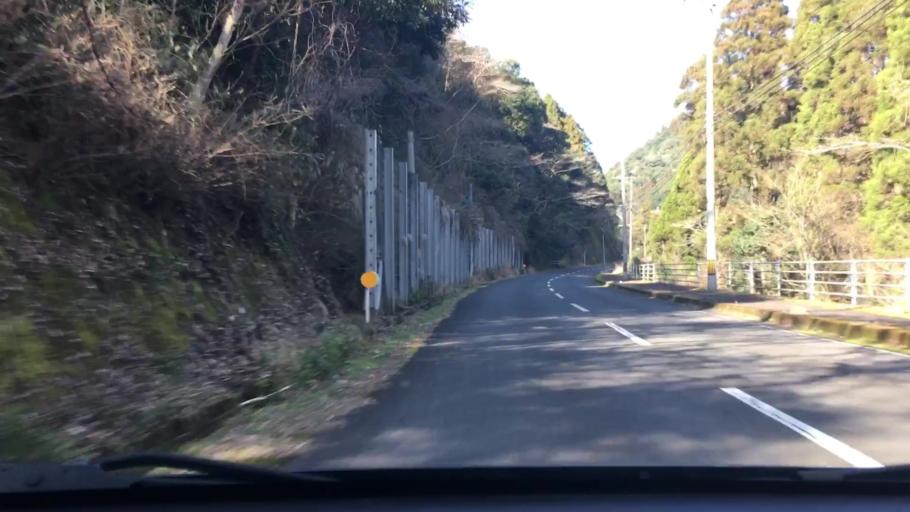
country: JP
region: Kagoshima
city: Satsumasendai
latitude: 31.7506
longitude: 130.4111
